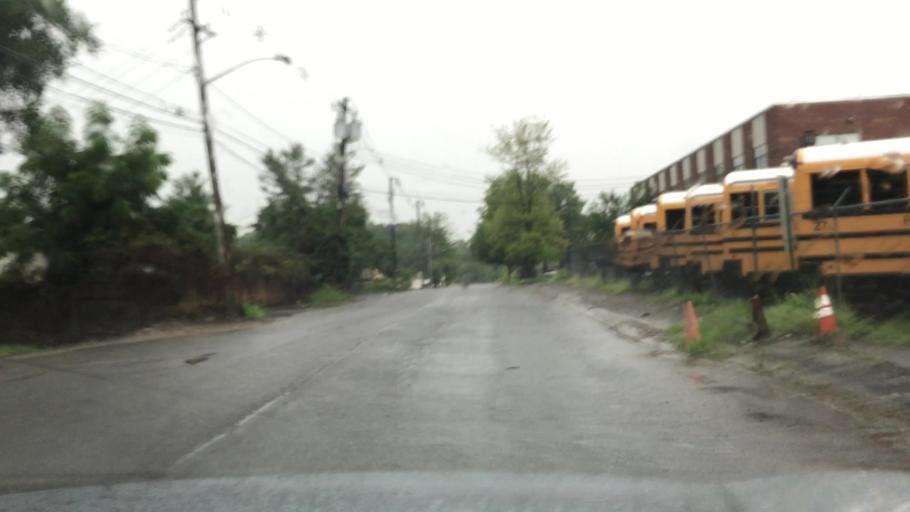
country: US
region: New Jersey
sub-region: Bergen County
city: Closter
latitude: 40.9777
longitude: -73.9606
